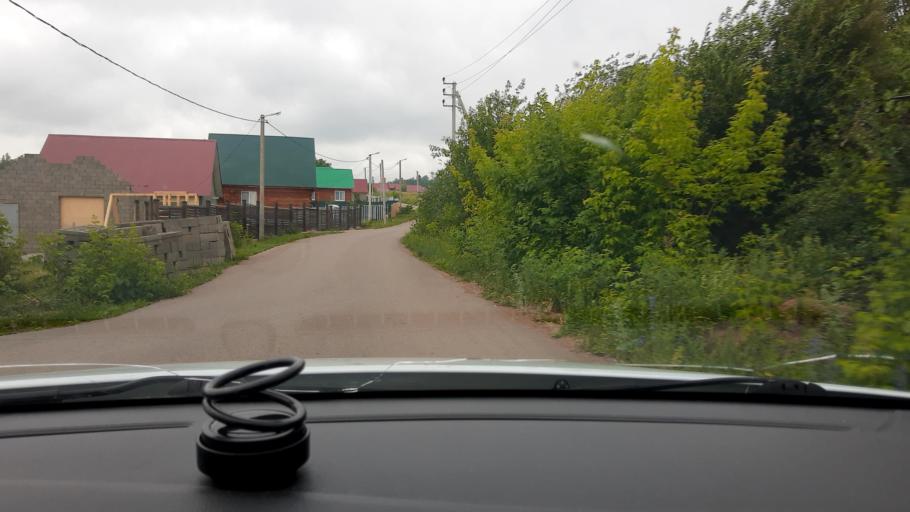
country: RU
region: Bashkortostan
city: Avdon
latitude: 54.6247
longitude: 55.6063
